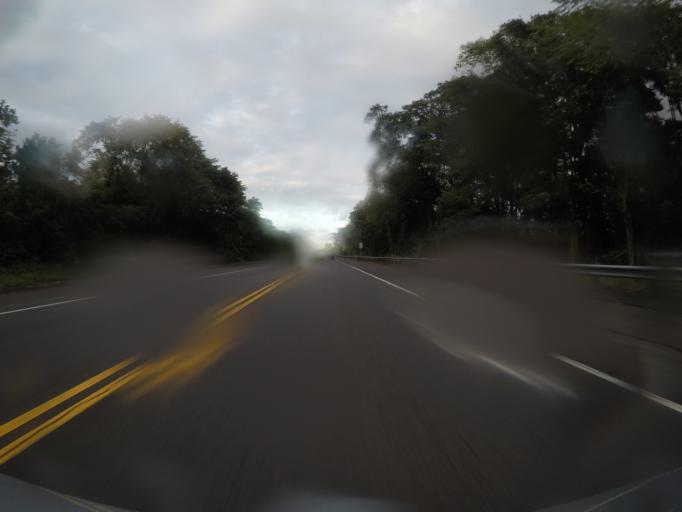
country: US
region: Hawaii
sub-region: Hawaii County
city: Hilo
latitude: 19.6938
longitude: -155.0960
